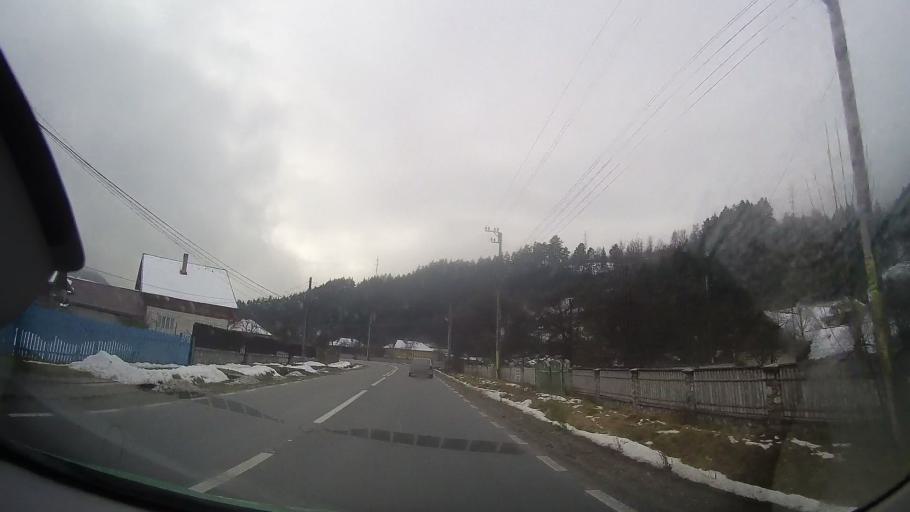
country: RO
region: Neamt
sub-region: Comuna Bicazu Ardelean
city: Bicazu Ardelean
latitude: 46.8633
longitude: 25.9386
